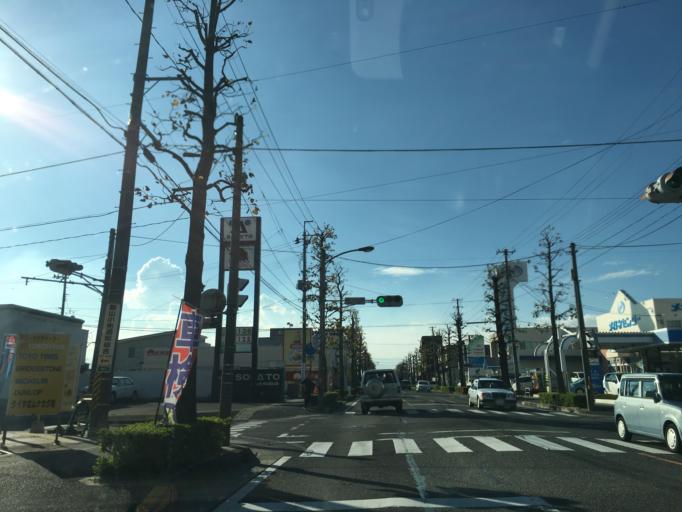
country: JP
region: Fukushima
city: Koriyama
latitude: 37.3985
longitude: 140.3396
